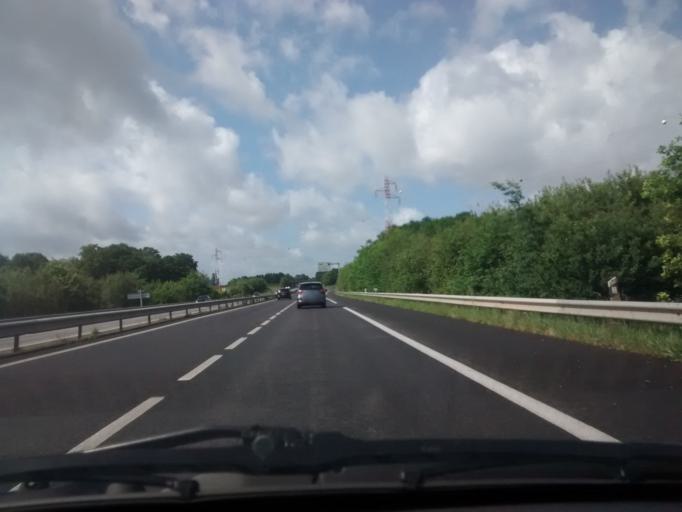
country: FR
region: Brittany
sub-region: Departement d'Ille-et-Vilaine
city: Le Rheu
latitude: 48.0835
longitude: -1.7878
